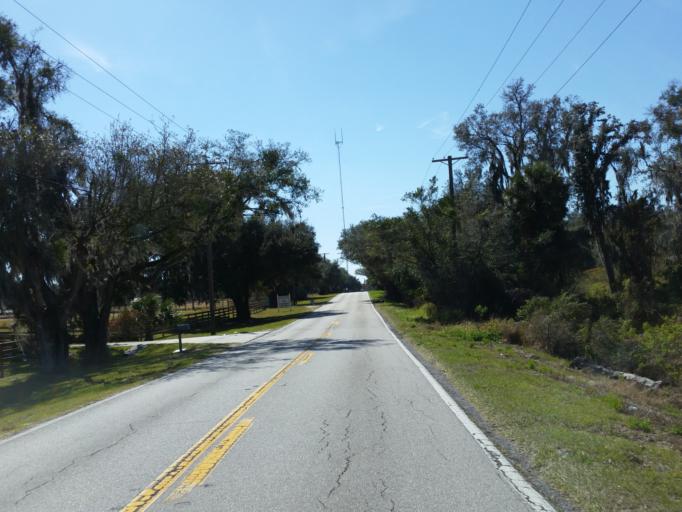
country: US
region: Florida
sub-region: Hillsborough County
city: Boyette
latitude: 27.8388
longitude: -82.2610
